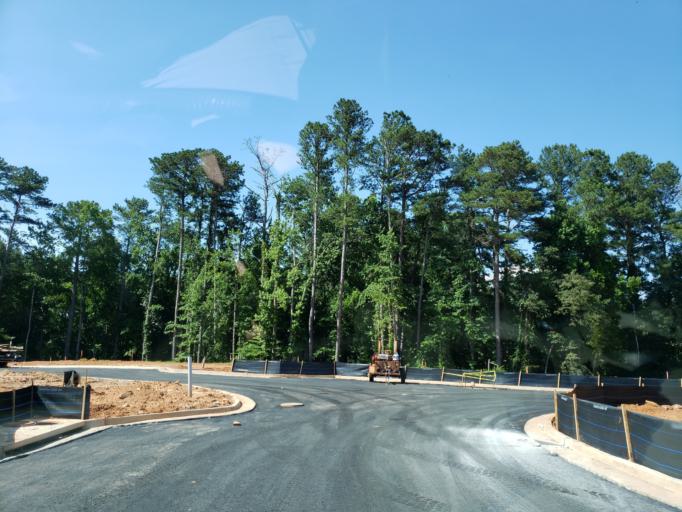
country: US
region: Georgia
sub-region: Fulton County
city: Alpharetta
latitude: 34.0932
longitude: -84.3357
